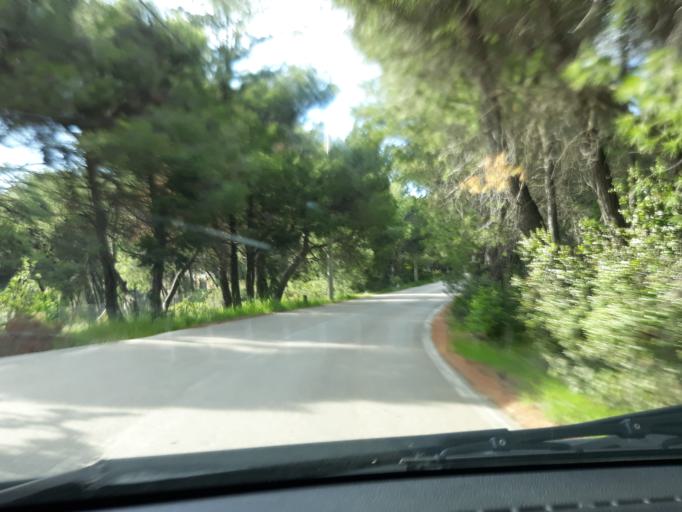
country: GR
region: Attica
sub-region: Nomarchia Anatolikis Attikis
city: Varybobi
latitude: 38.1345
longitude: 23.7920
